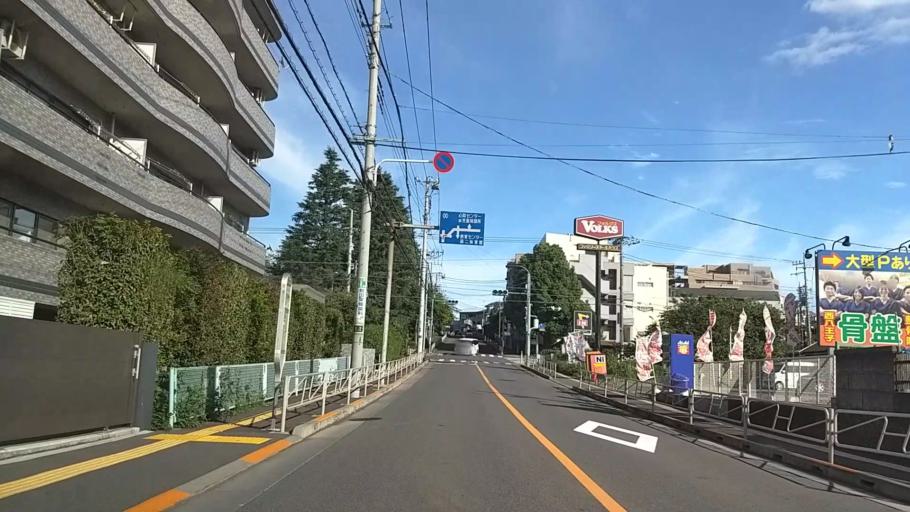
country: JP
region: Tokyo
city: Hachioji
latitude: 35.6516
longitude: 139.3195
